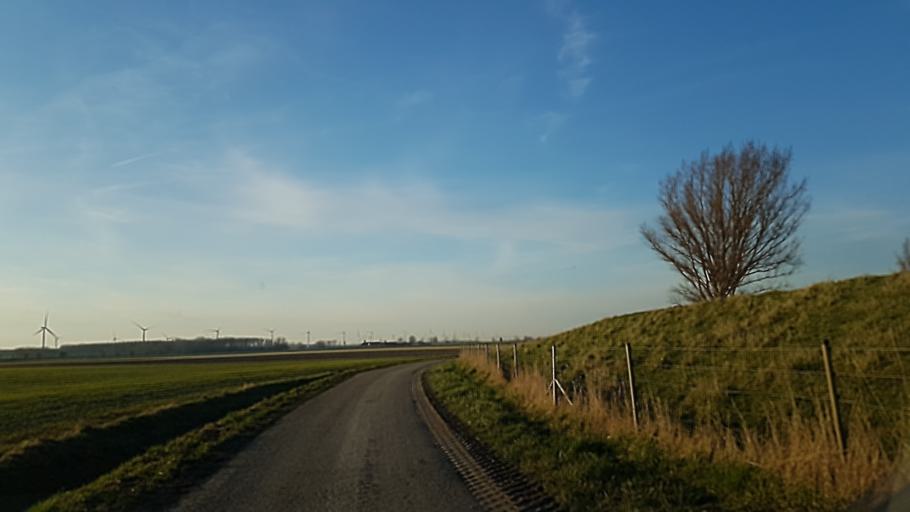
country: NL
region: North Brabant
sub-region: Gemeente Woensdrecht
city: Woensdrecht
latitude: 51.3914
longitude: 4.2686
